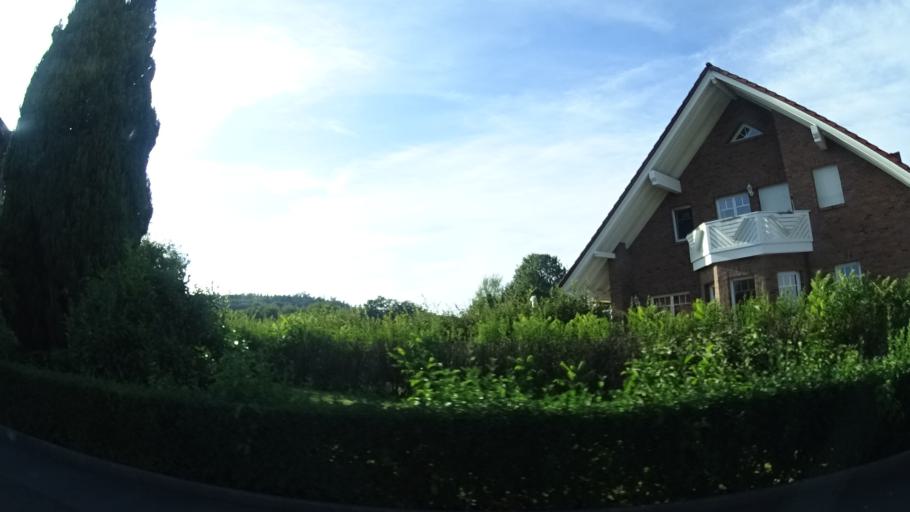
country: DE
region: Hesse
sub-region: Regierungsbezirk Kassel
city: Flieden
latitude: 50.4443
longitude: 9.5779
